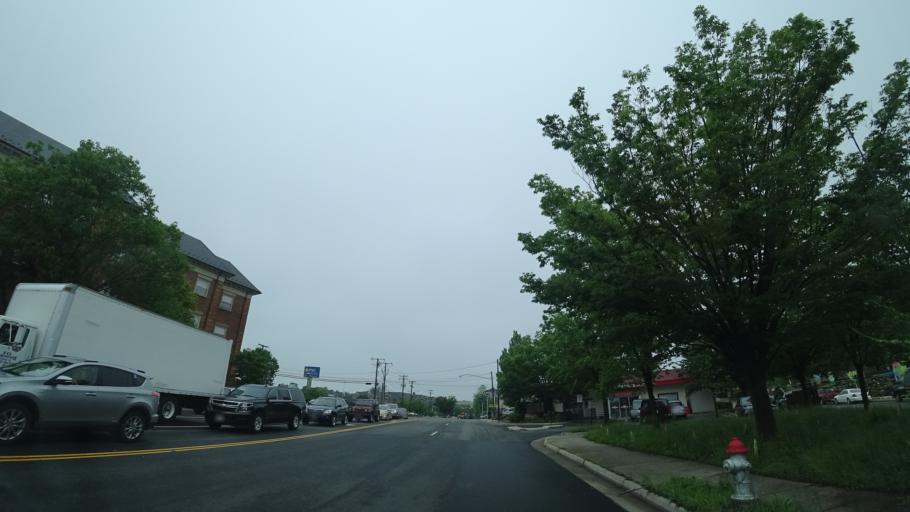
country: US
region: Virginia
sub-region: Fairfax County
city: McLean
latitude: 38.9343
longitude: -77.1775
